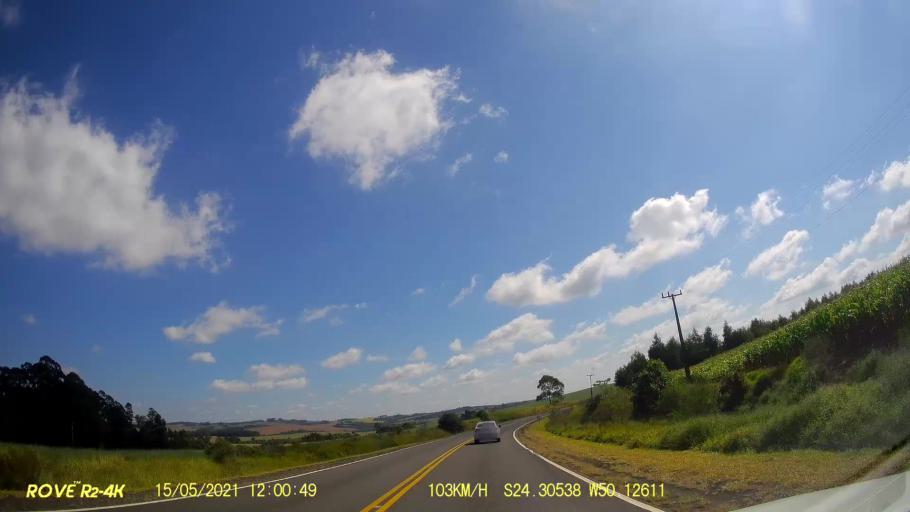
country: BR
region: Parana
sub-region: Pirai Do Sul
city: Pirai do Sul
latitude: -24.3056
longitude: -50.1260
